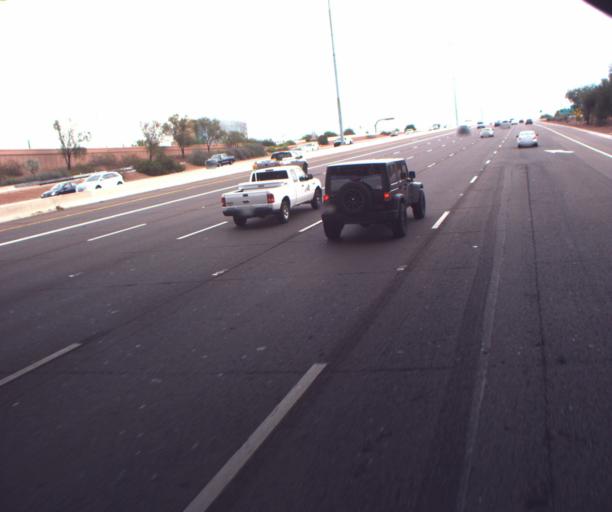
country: US
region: Arizona
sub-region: Maricopa County
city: Tempe Junction
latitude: 33.4359
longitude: -111.9496
